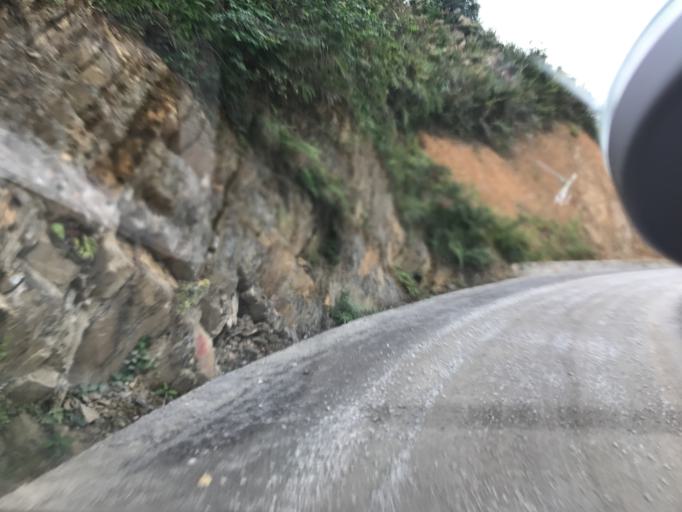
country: CN
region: Guizhou Sheng
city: Donghua
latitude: 28.0609
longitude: 108.1049
